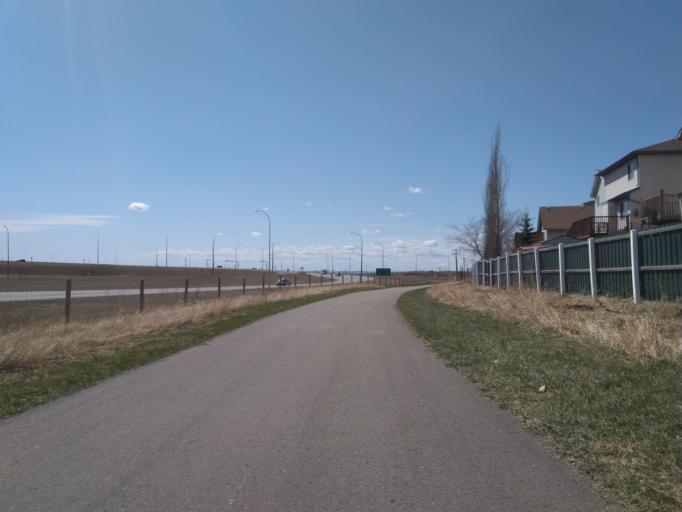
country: CA
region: Alberta
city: Chestermere
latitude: 51.0410
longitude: -113.9232
